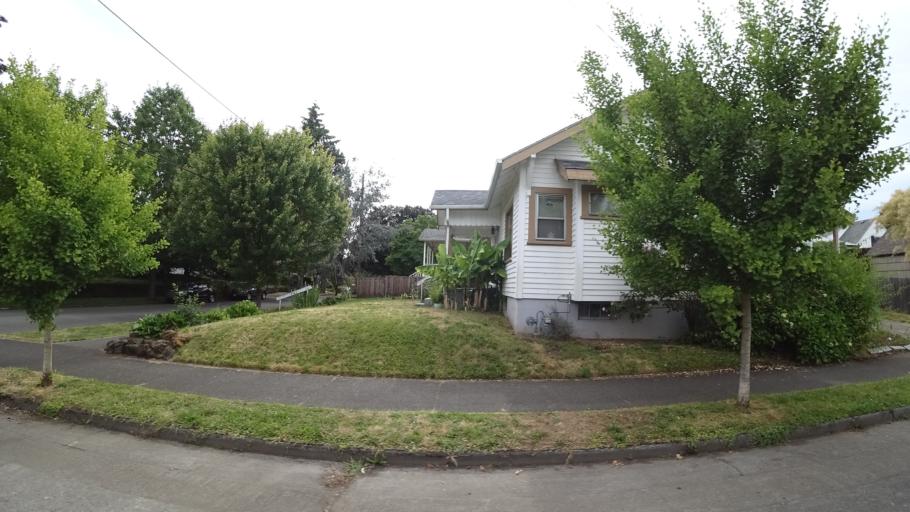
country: US
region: Oregon
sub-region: Multnomah County
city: Portland
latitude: 45.5614
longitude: -122.6926
